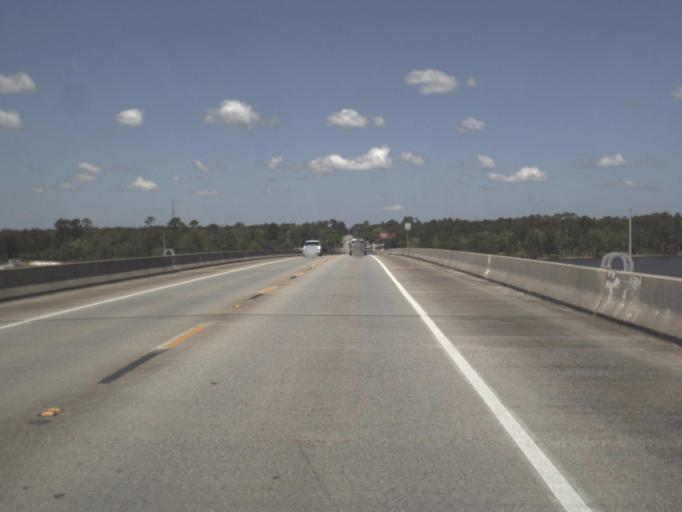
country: US
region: Florida
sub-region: Escambia County
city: Myrtle Grove
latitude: 30.4050
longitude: -87.4309
